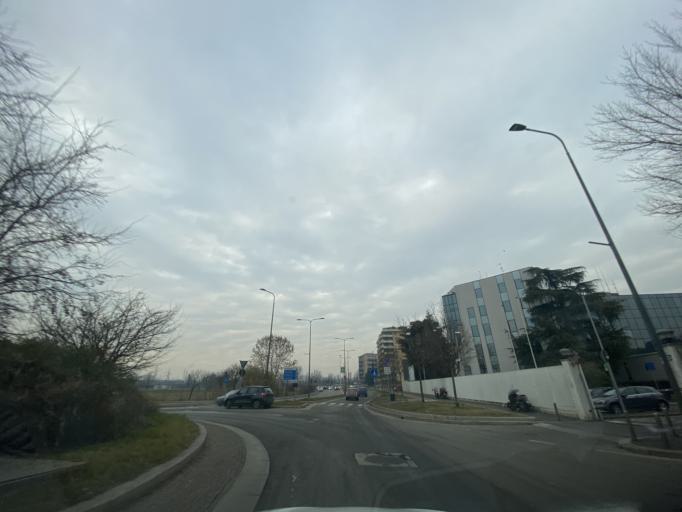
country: IT
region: Lombardy
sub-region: Citta metropolitana di Milano
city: Vimodrone
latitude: 45.5097
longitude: 9.2670
